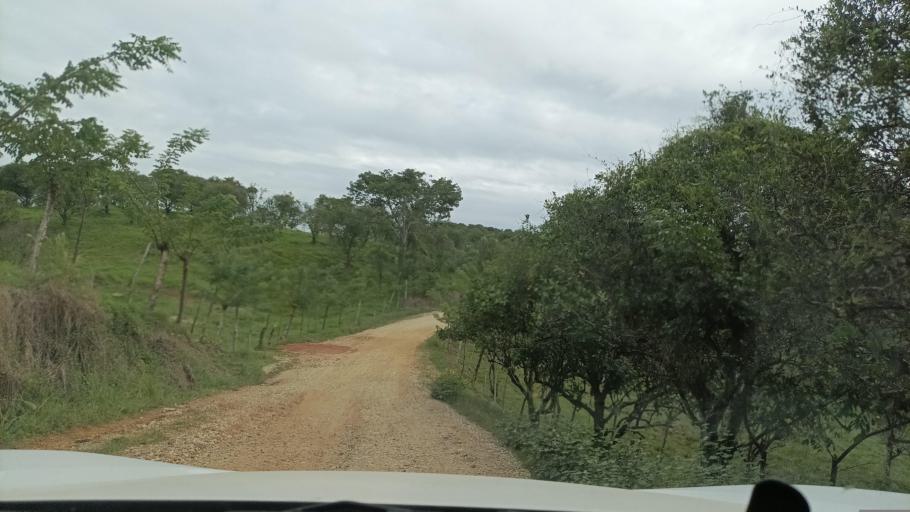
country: MX
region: Veracruz
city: Hidalgotitlan
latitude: 17.6025
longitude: -94.4255
